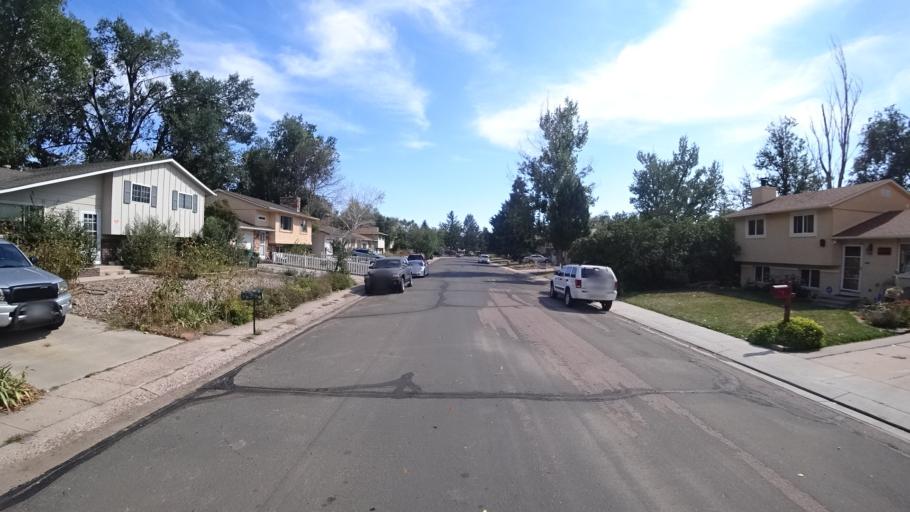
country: US
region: Colorado
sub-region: El Paso County
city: Cimarron Hills
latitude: 38.8976
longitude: -104.7596
